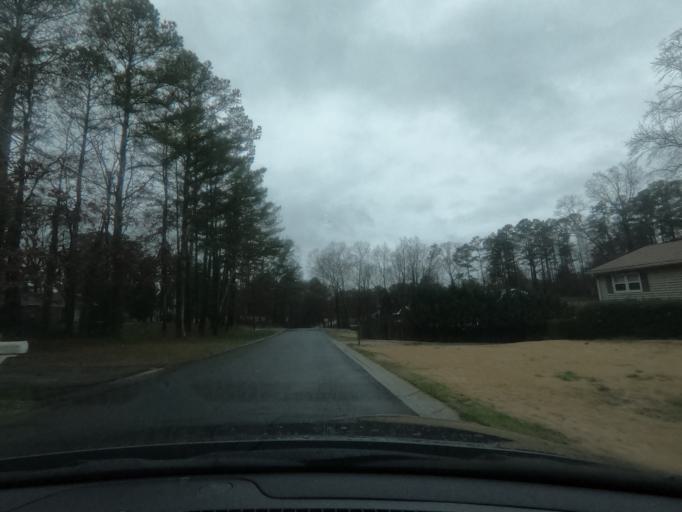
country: US
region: Georgia
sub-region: Cherokee County
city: Woodstock
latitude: 34.1016
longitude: -84.4959
